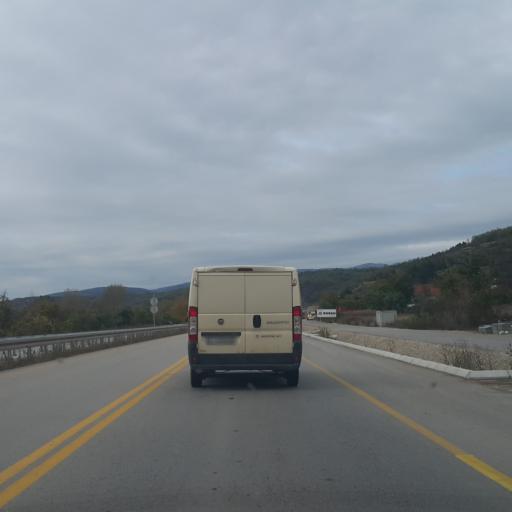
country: RS
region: Central Serbia
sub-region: Pirotski Okrug
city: Pirot
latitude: 43.2267
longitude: 22.4677
